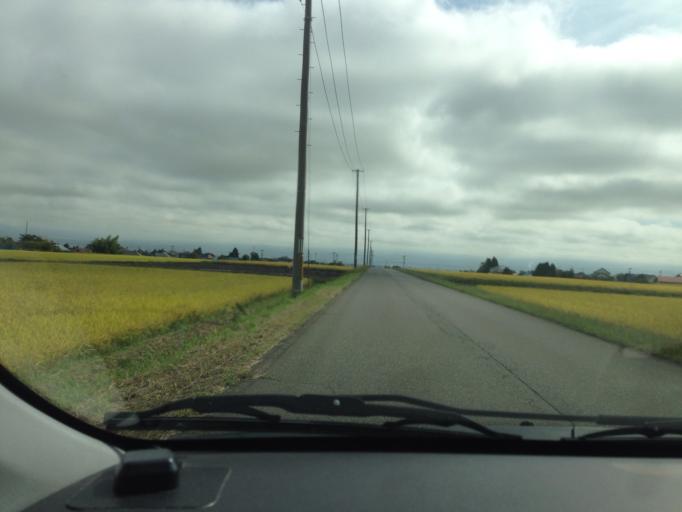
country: JP
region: Fukushima
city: Kitakata
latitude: 37.5234
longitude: 139.8147
